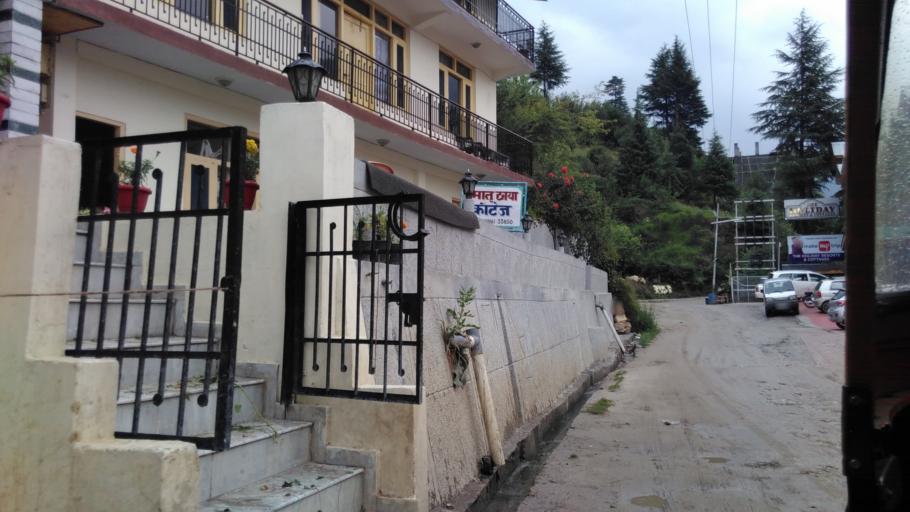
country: IN
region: Himachal Pradesh
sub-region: Kulu
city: Manali
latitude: 32.2242
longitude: 77.1846
